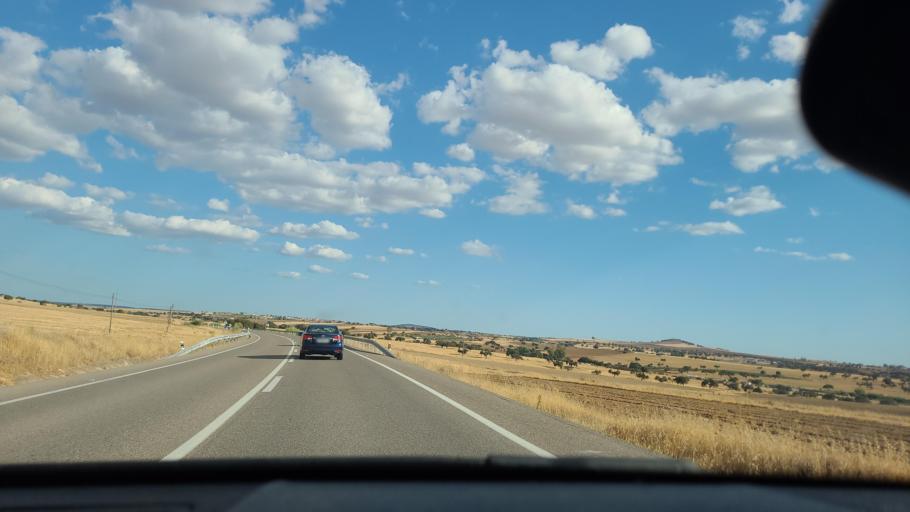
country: ES
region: Extremadura
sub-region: Provincia de Badajoz
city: Granja de Torrehermosa
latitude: 38.2763
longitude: -5.5156
